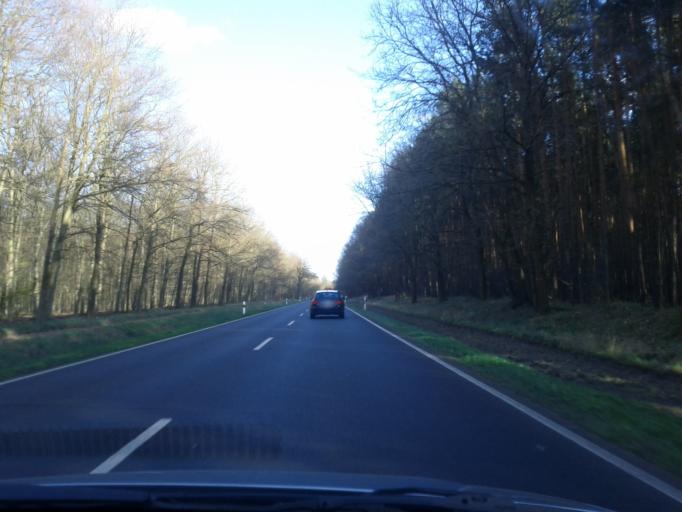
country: DE
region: Brandenburg
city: Rauen
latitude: 52.3754
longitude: 13.9982
